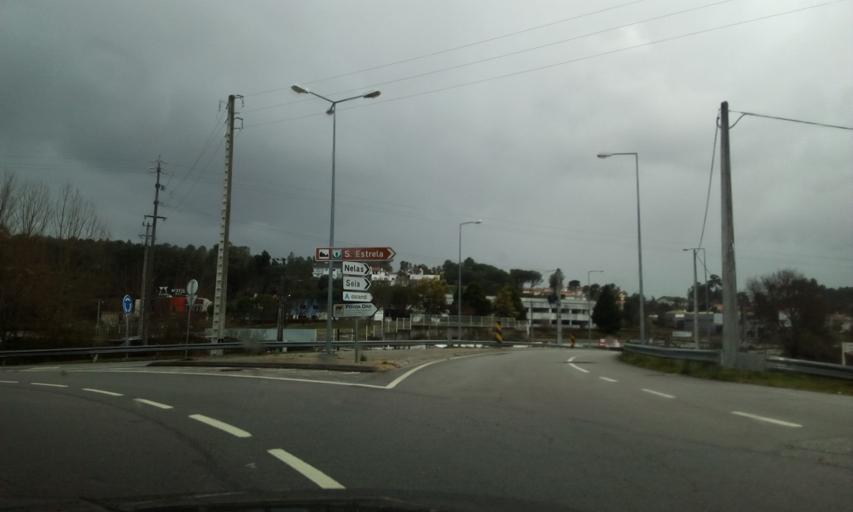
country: PT
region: Viseu
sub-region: Viseu
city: Viseu
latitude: 40.6224
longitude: -7.9191
